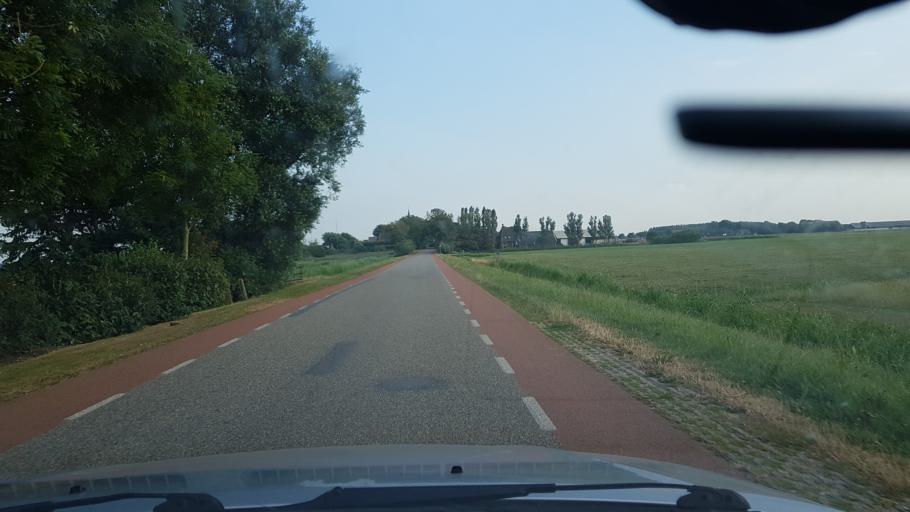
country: NL
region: Friesland
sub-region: Gemeente Ferwerderadiel
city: Burdaard
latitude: 53.3163
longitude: 5.8767
